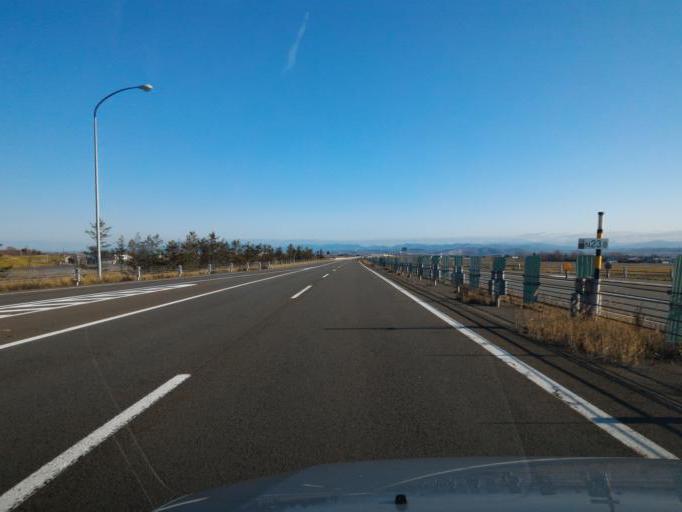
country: JP
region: Hokkaido
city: Iwamizawa
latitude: 43.1429
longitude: 141.6772
